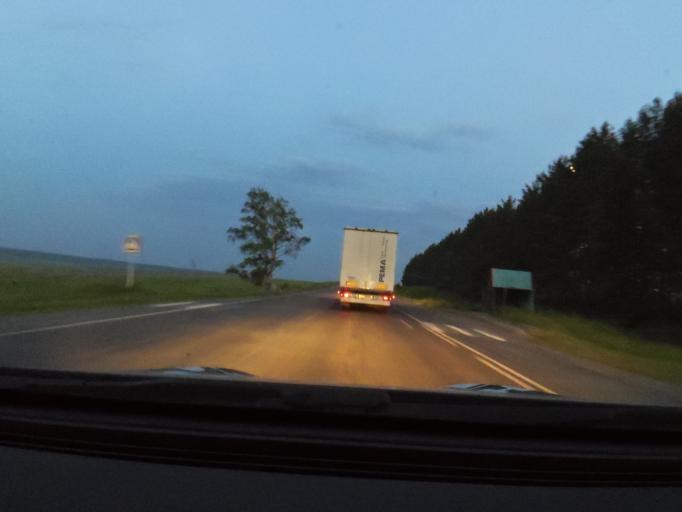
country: RU
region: Bashkortostan
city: Duvan
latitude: 56.0479
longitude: 58.2013
